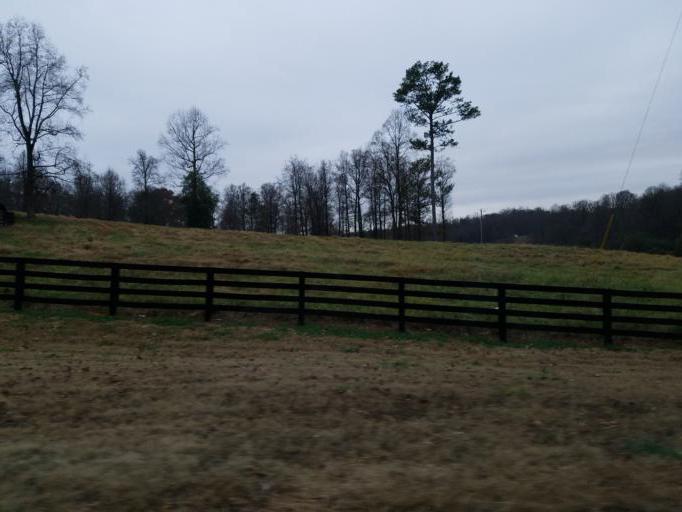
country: US
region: Georgia
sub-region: Dawson County
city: Dawsonville
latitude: 34.4719
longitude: -84.1526
